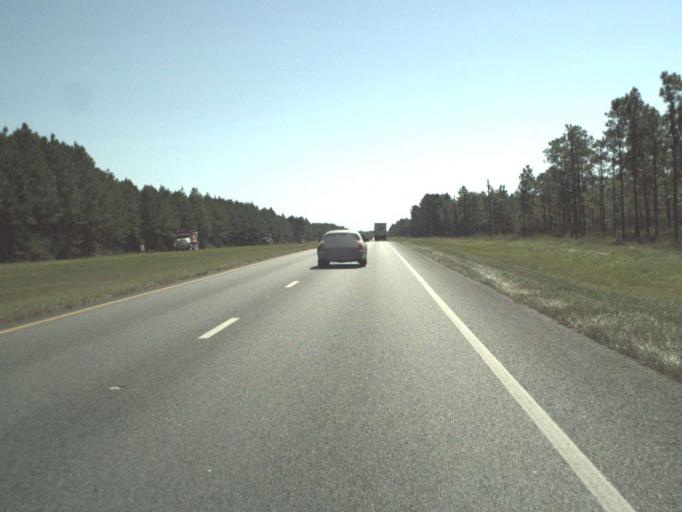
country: US
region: Florida
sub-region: Walton County
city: Seaside
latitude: 30.3449
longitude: -86.0749
